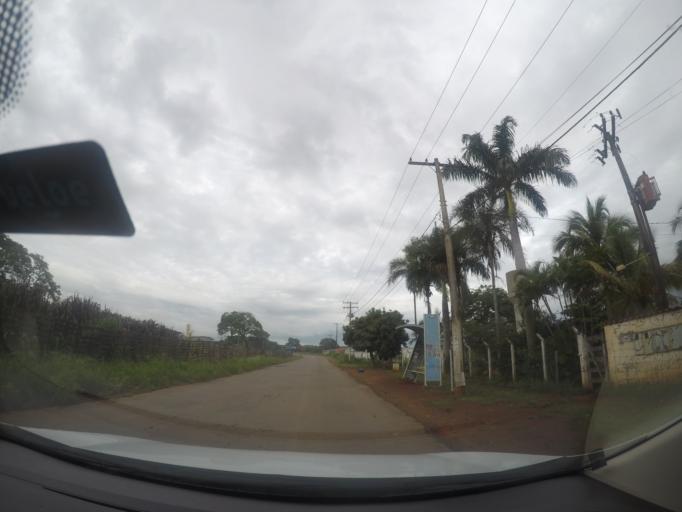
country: BR
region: Goias
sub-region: Goiania
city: Goiania
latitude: -16.6379
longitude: -49.3391
